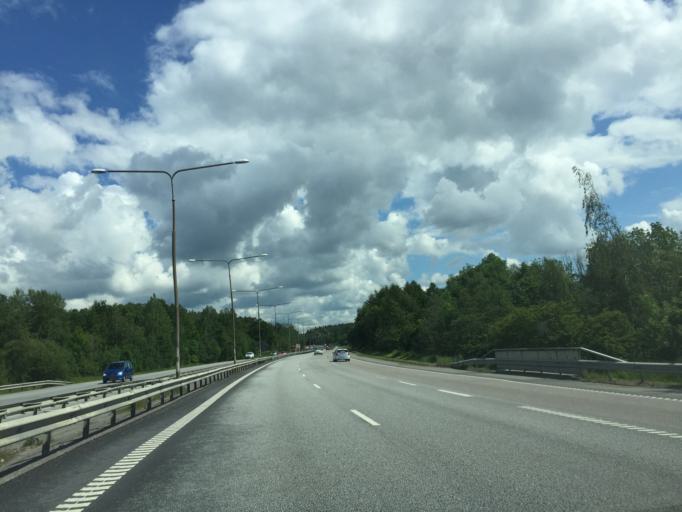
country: SE
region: Vaestmanland
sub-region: Vasteras
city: Vasteras
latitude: 59.6123
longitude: 16.4790
